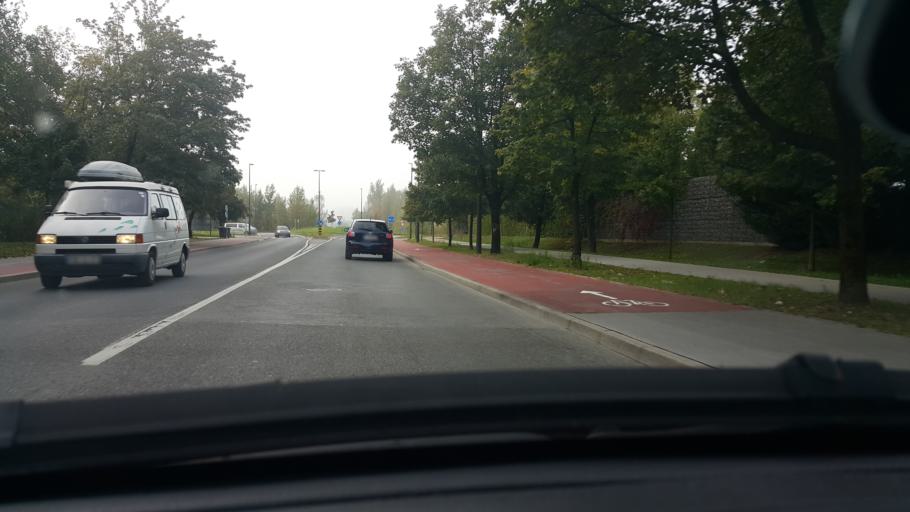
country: SI
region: Ljubljana
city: Ljubljana
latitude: 46.0630
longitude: 14.5499
